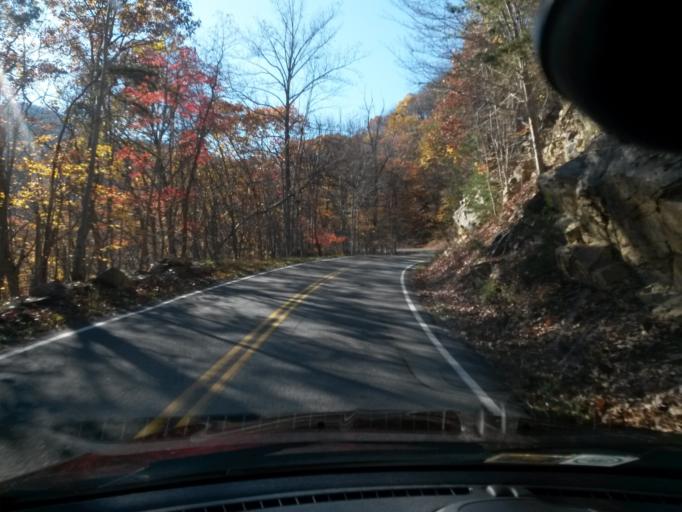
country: US
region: Virginia
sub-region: Botetourt County
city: Buchanan
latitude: 37.5043
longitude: -79.6649
